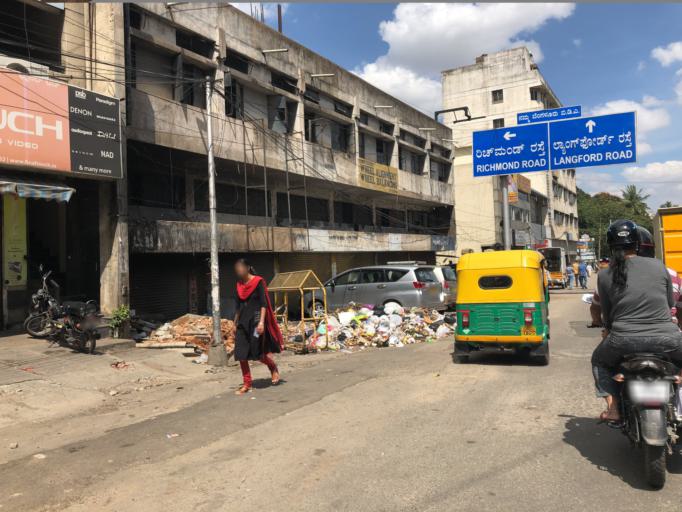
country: IN
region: Karnataka
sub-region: Bangalore Urban
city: Bangalore
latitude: 12.9627
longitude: 77.5907
